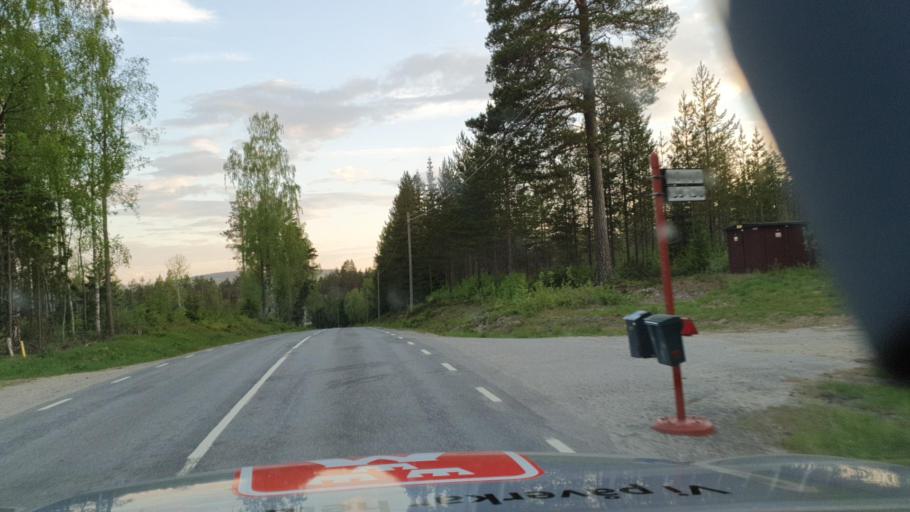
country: SE
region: Vaesternorrland
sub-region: OErnskoeldsviks Kommun
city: Bjasta
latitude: 63.2062
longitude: 18.5414
